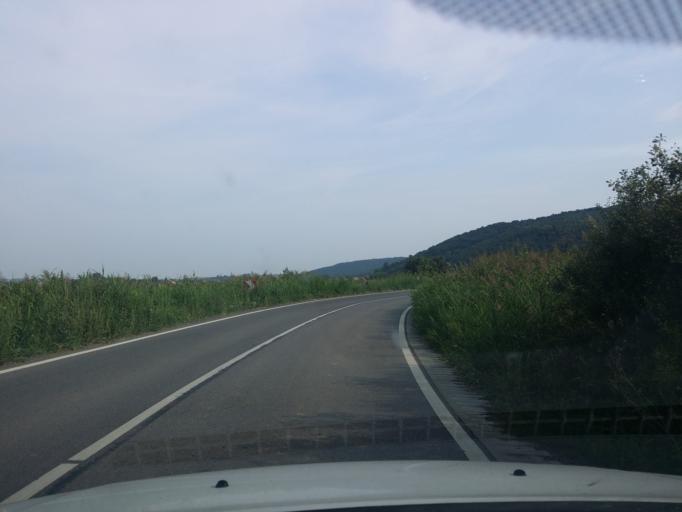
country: HU
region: Pest
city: Acsa
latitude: 47.7593
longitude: 19.3681
